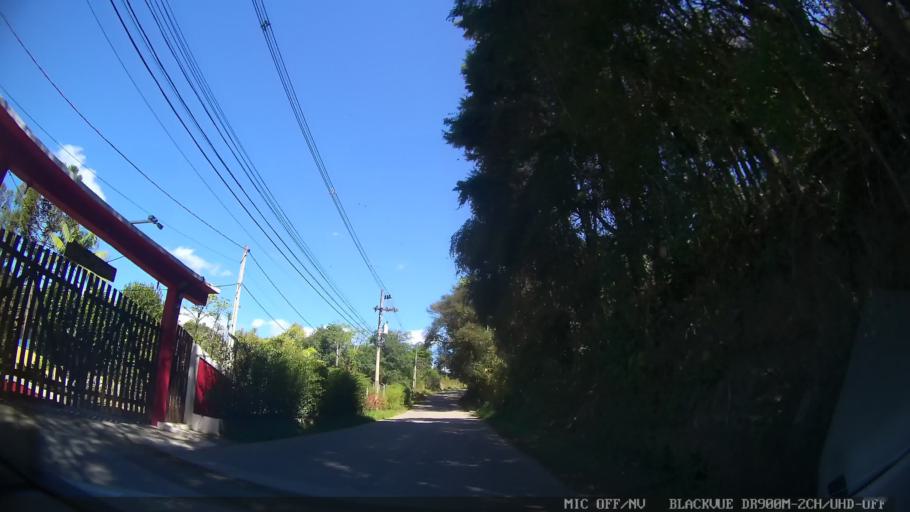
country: BR
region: Sao Paulo
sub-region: Campo Limpo Paulista
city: Campo Limpo Paulista
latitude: -23.1732
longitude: -46.7387
